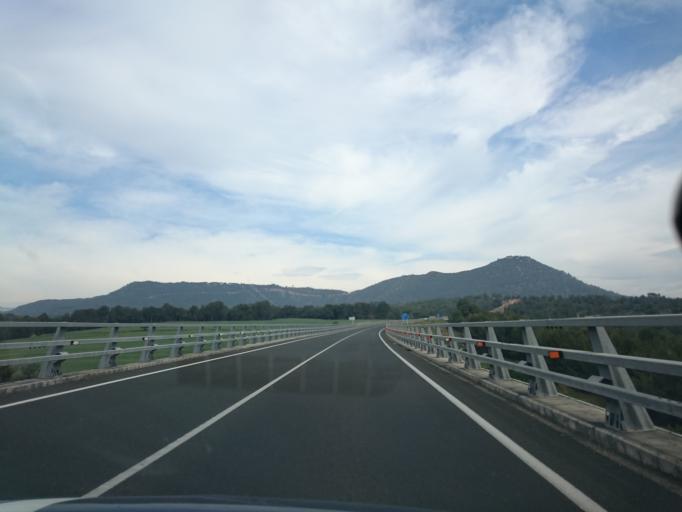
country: ES
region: Catalonia
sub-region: Provincia de Barcelona
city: Sant Joan de Vilatorrada
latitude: 41.7203
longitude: 1.7827
